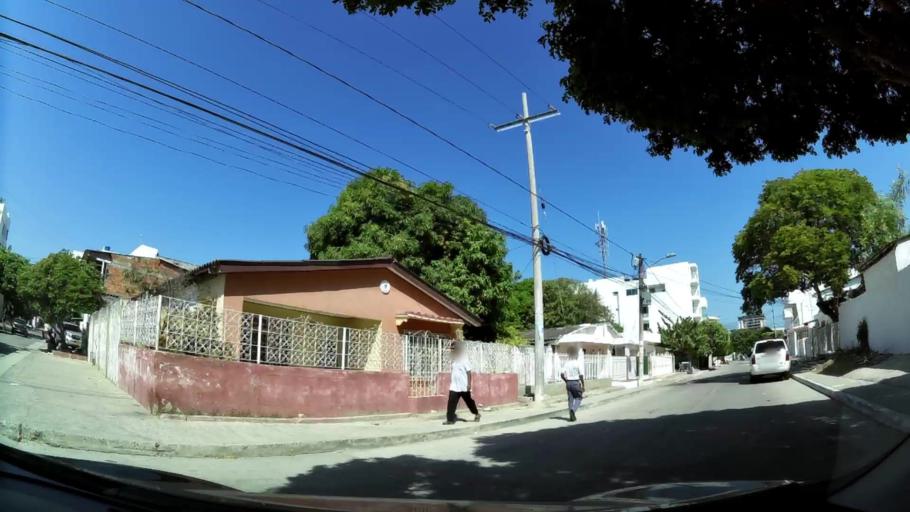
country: CO
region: Bolivar
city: Cartagena
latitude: 10.4390
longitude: -75.5249
